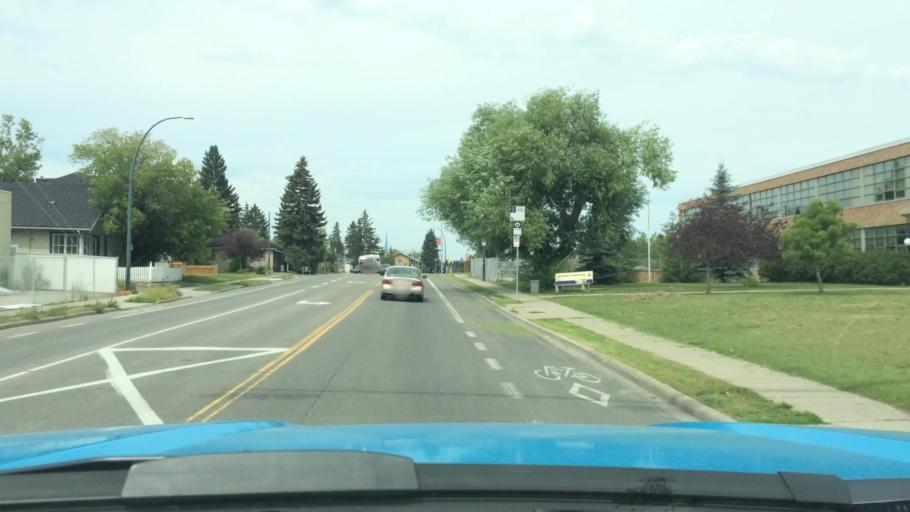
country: CA
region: Alberta
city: Calgary
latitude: 51.0706
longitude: -114.0848
